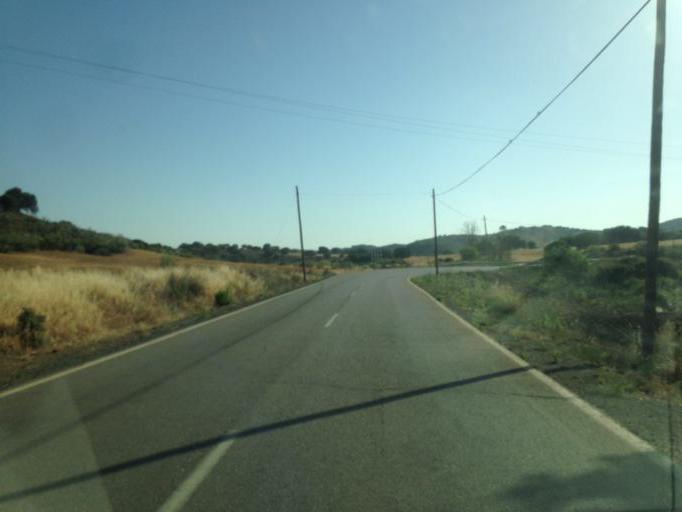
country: ES
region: Andalusia
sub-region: Provincia de Malaga
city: Archidona
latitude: 37.1055
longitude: -4.3572
